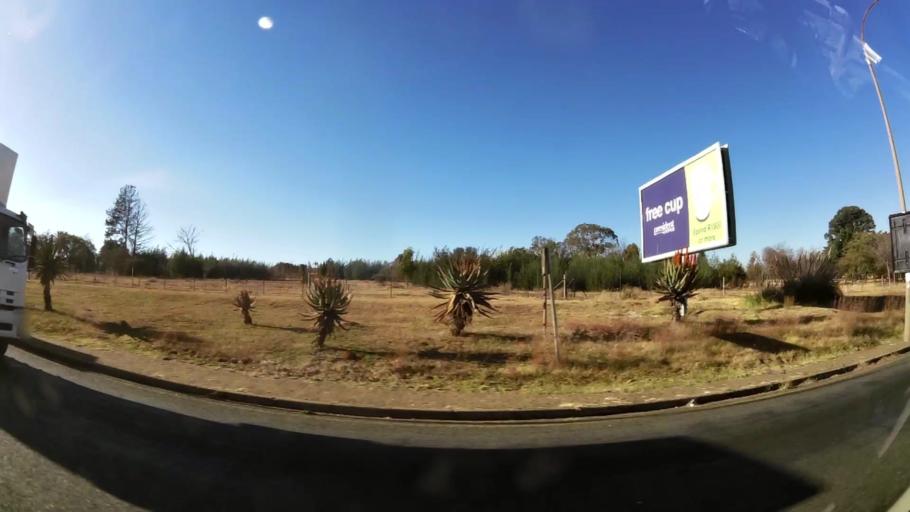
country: ZA
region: Gauteng
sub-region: West Rand District Municipality
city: Krugersdorp
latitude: -26.0916
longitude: 27.7795
